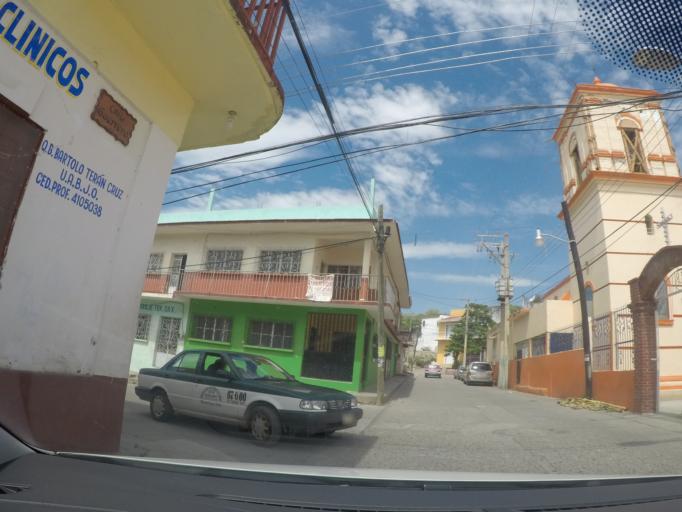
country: MX
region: Oaxaca
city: San Blas Atempa
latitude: 16.3345
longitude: -95.2281
